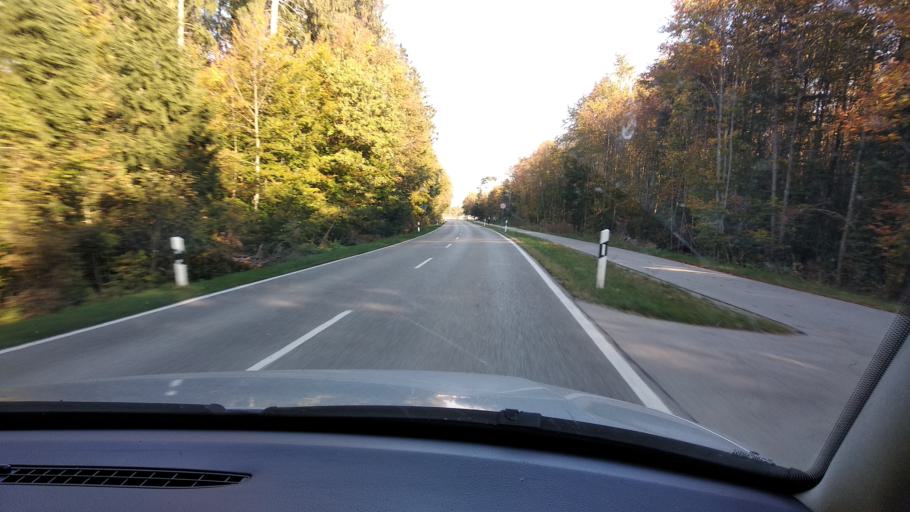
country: DE
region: Bavaria
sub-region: Upper Bavaria
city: Egmating
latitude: 48.0138
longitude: 11.7636
